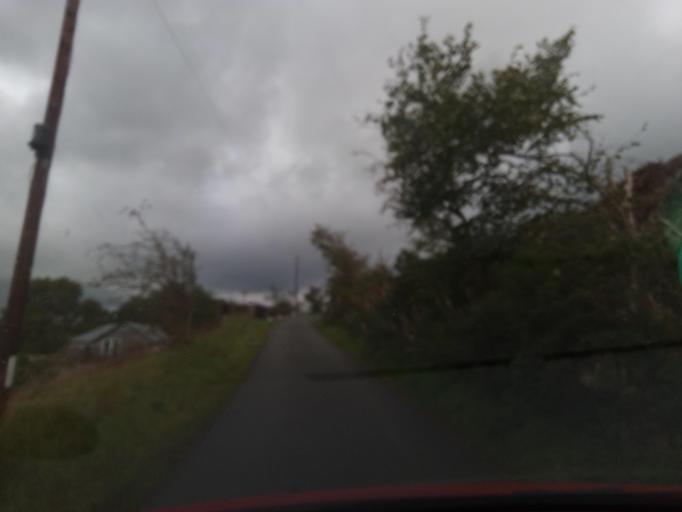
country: GB
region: Scotland
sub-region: The Scottish Borders
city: Coldstream
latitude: 55.5453
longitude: -2.2704
